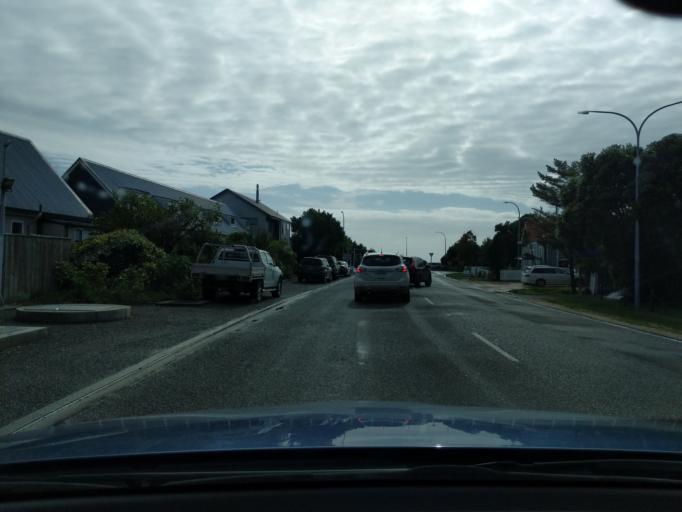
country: NZ
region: Tasman
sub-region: Tasman District
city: Takaka
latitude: -40.6776
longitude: 172.6818
